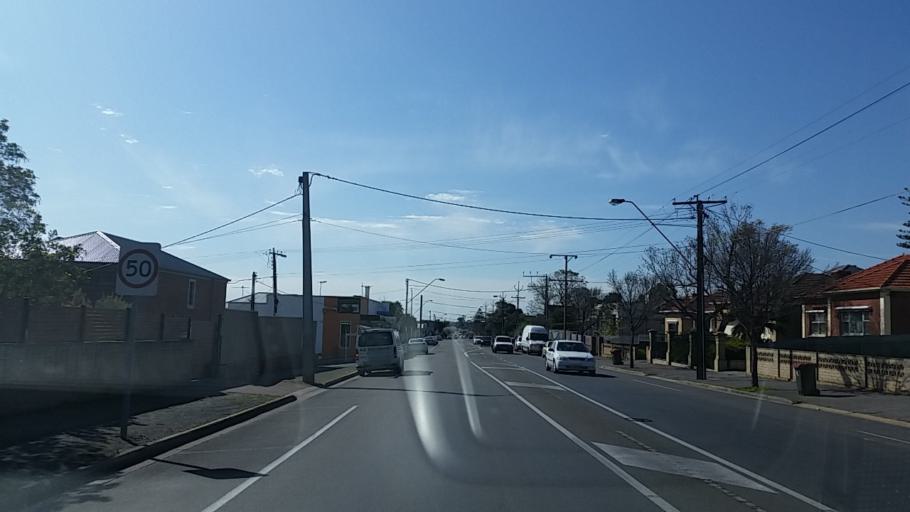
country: AU
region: South Australia
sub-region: Prospect
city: Prospect
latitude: -34.8732
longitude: 138.5930
